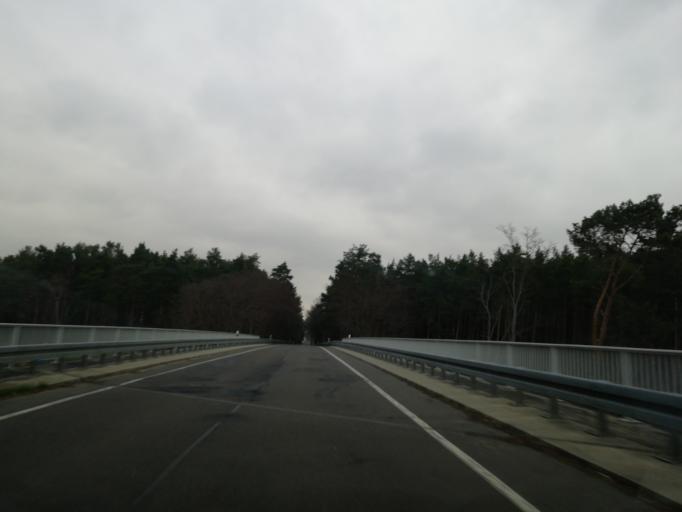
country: DE
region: Brandenburg
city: Vetschau
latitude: 51.7603
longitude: 14.1303
